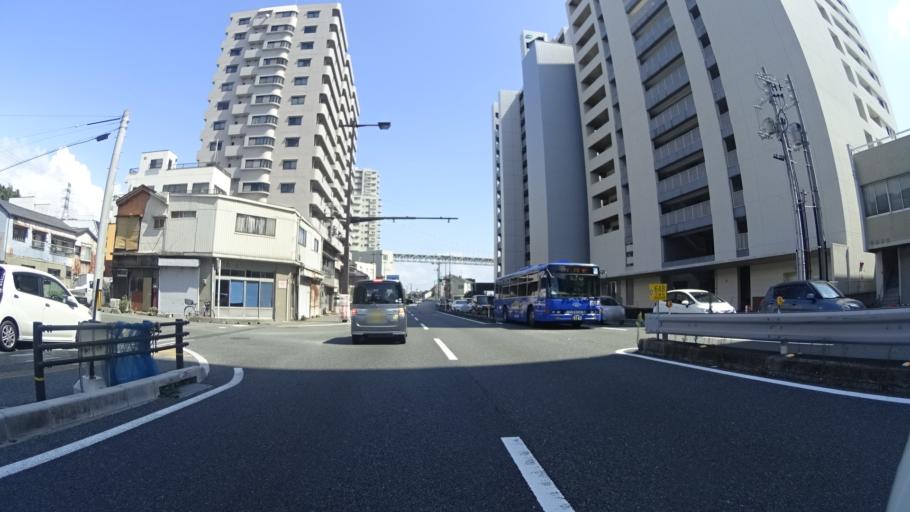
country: JP
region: Yamaguchi
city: Shimonoseki
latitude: 33.9597
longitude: 130.9502
